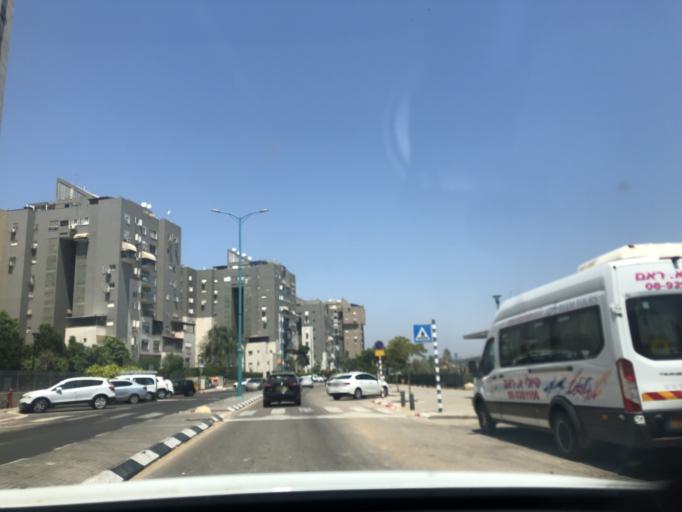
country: IL
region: Central District
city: Lod
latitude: 31.9439
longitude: 34.9034
